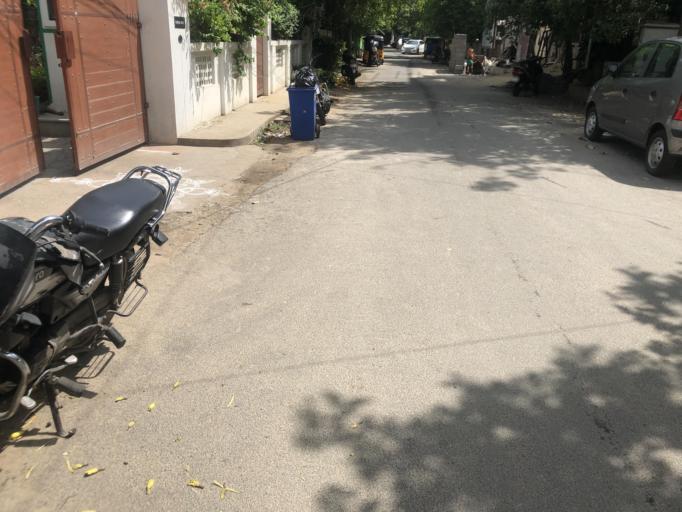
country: IN
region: Tamil Nadu
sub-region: Chennai
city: Gandhi Nagar
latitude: 13.0385
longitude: 80.2653
